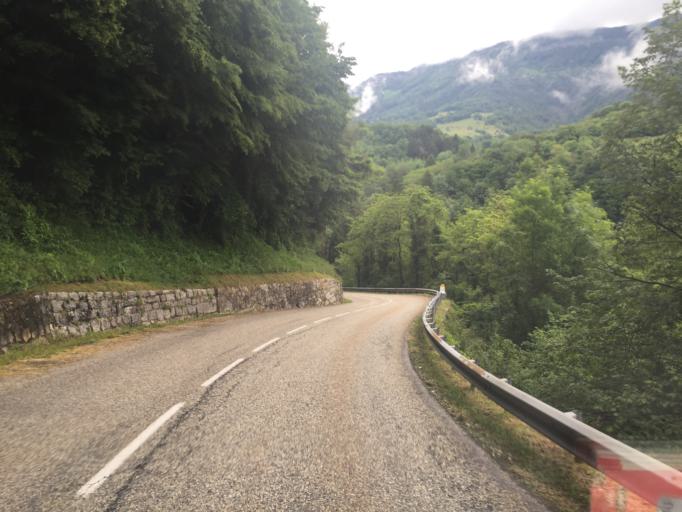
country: FR
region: Rhone-Alpes
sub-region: Departement de la Savoie
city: Barby
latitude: 45.5900
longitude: 6.0196
